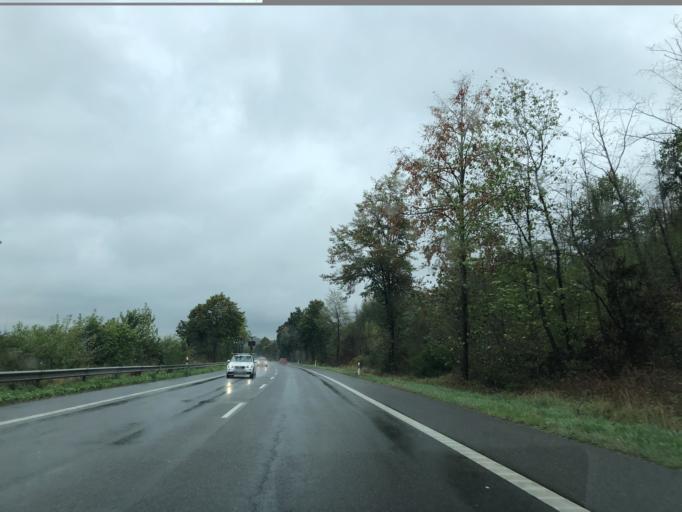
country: DE
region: North Rhine-Westphalia
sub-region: Regierungsbezirk Dusseldorf
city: Grevenbroich
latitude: 51.0693
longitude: 6.5571
